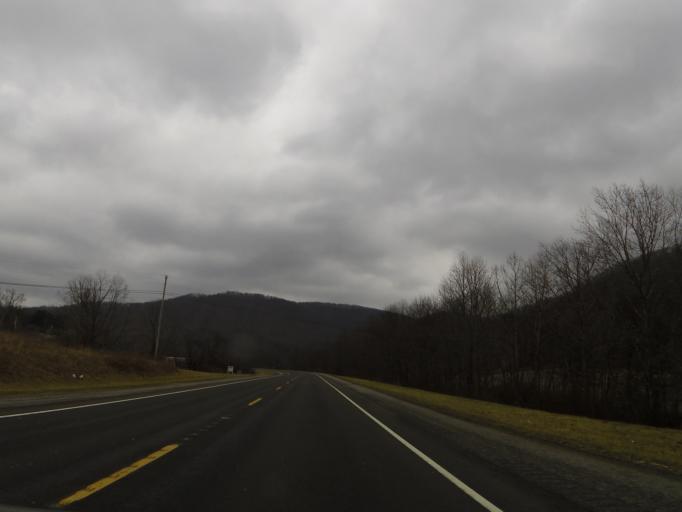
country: US
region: Tennessee
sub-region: Scott County
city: Huntsville
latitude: 36.3792
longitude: -84.3523
